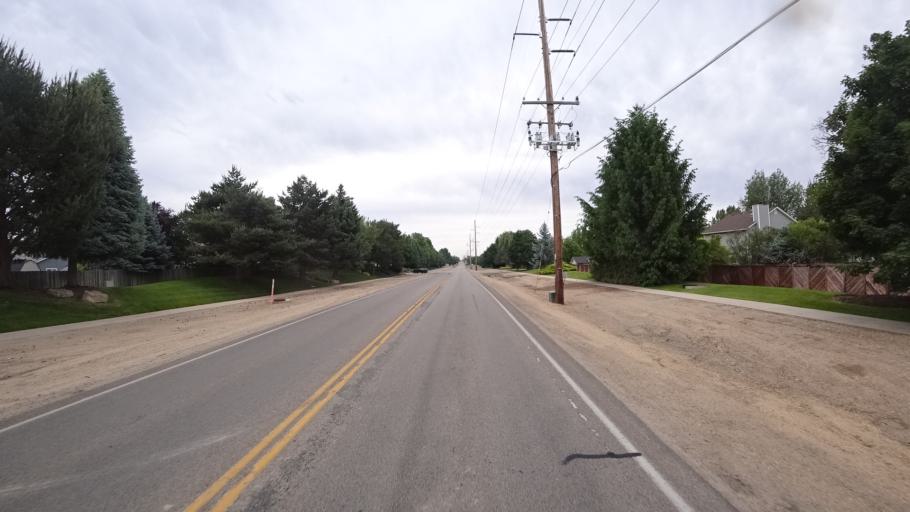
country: US
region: Idaho
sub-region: Ada County
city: Meridian
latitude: 43.5879
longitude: -116.3344
